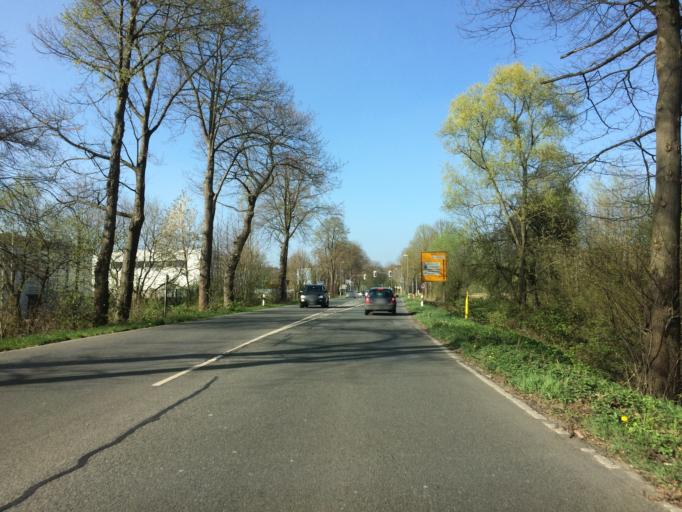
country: DE
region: North Rhine-Westphalia
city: Hattingen
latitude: 51.4209
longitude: 7.1683
